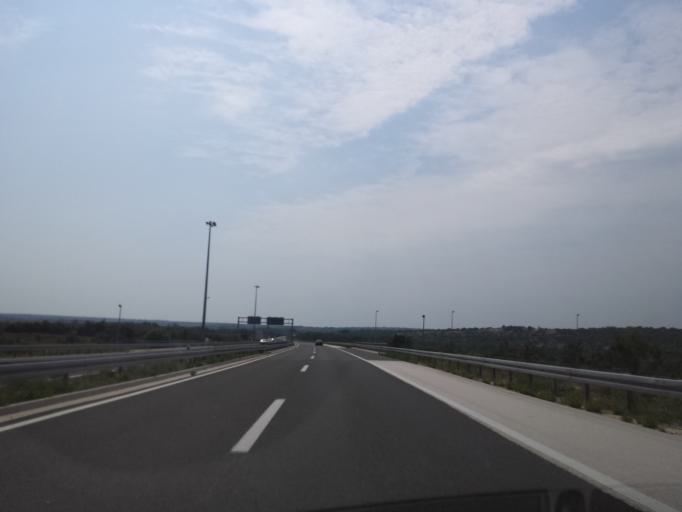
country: HR
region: Zadarska
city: Posedarje
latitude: 44.1874
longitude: 15.4331
